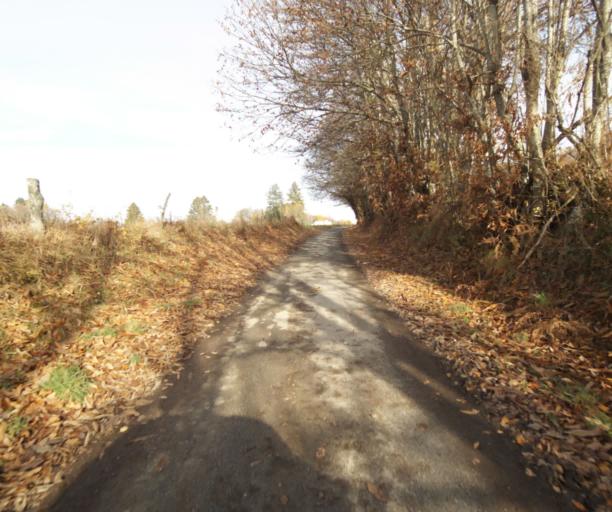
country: FR
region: Limousin
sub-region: Departement de la Correze
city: Sainte-Fortunade
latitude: 45.1977
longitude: 1.7469
